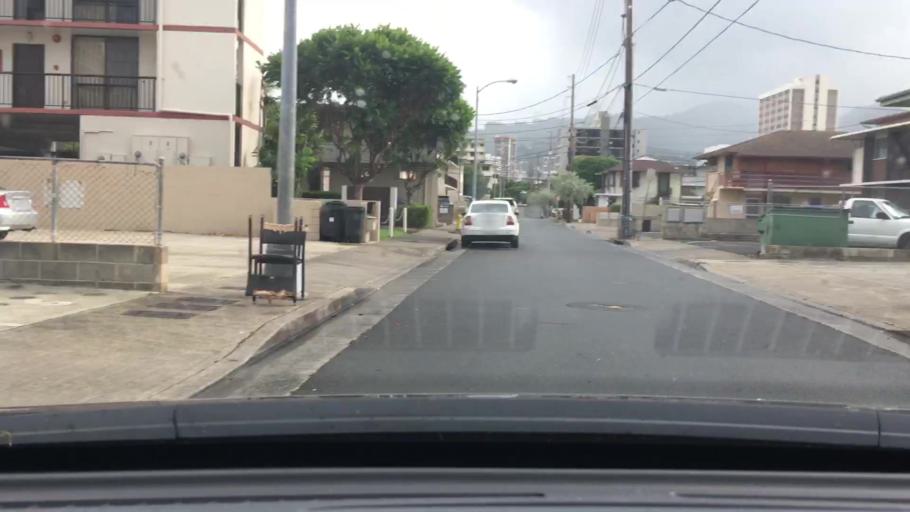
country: US
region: Hawaii
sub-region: Honolulu County
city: Honolulu
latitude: 21.2962
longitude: -157.8442
